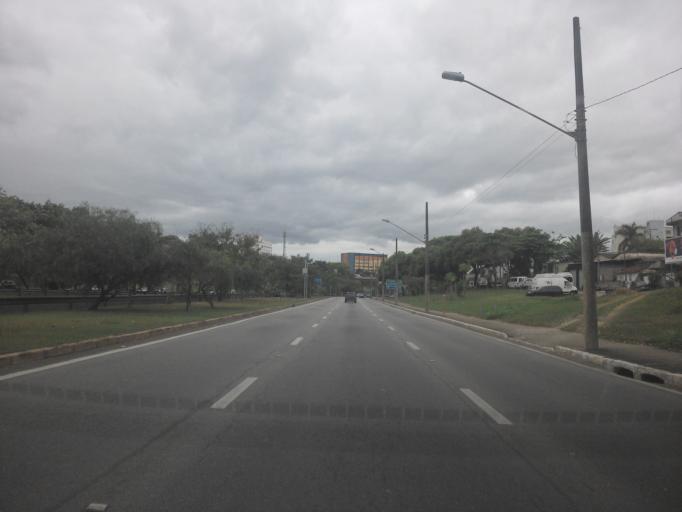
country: BR
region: Sao Paulo
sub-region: Sao Jose Dos Campos
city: Sao Jose dos Campos
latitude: -23.1903
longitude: -45.8821
